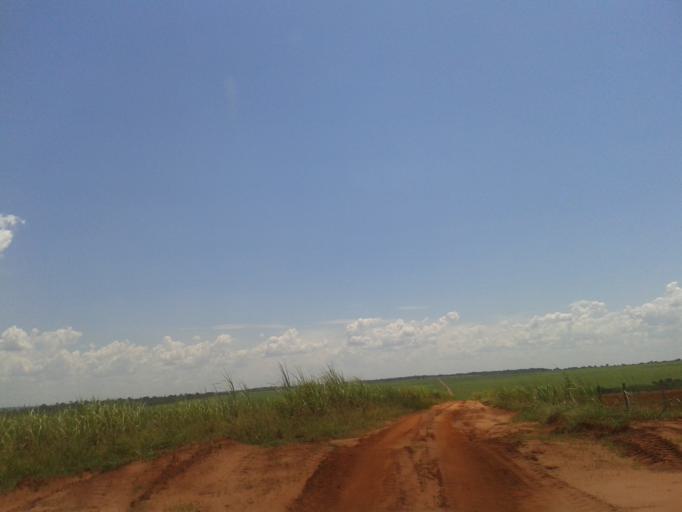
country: BR
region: Minas Gerais
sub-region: Santa Vitoria
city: Santa Vitoria
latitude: -19.1675
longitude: -50.4250
